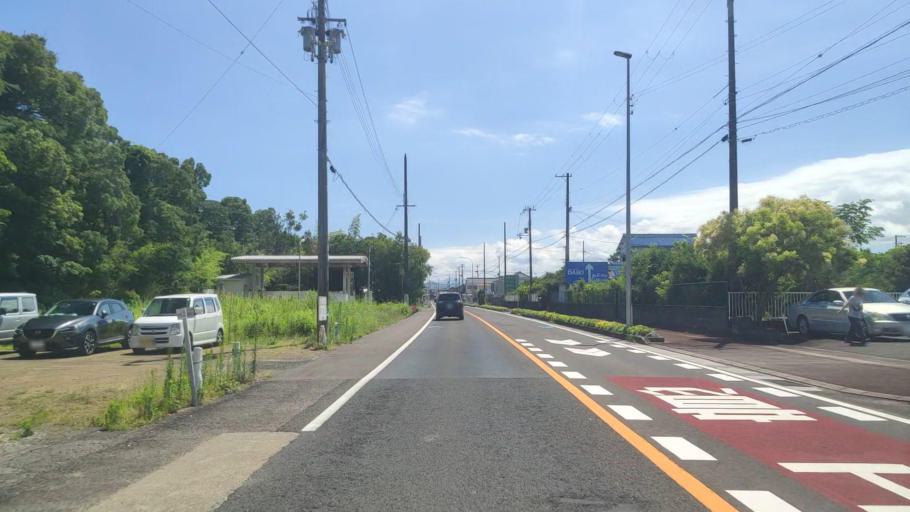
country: JP
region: Wakayama
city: Shingu
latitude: 33.8742
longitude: 136.0876
